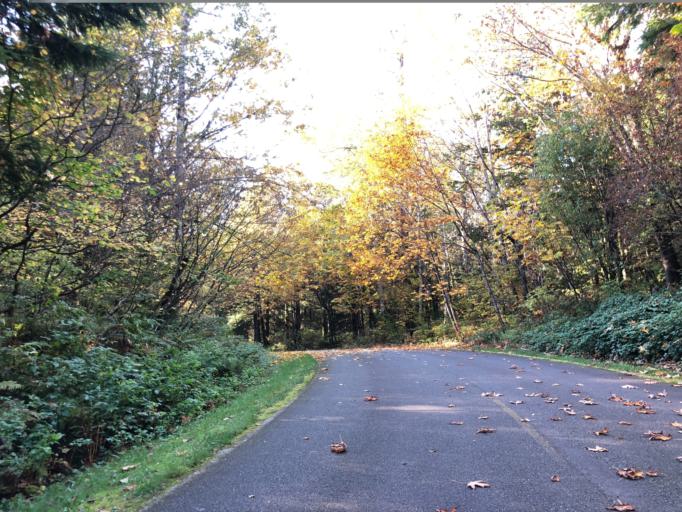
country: US
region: Washington
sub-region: King County
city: Ravensdale
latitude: 47.3188
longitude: -121.9017
